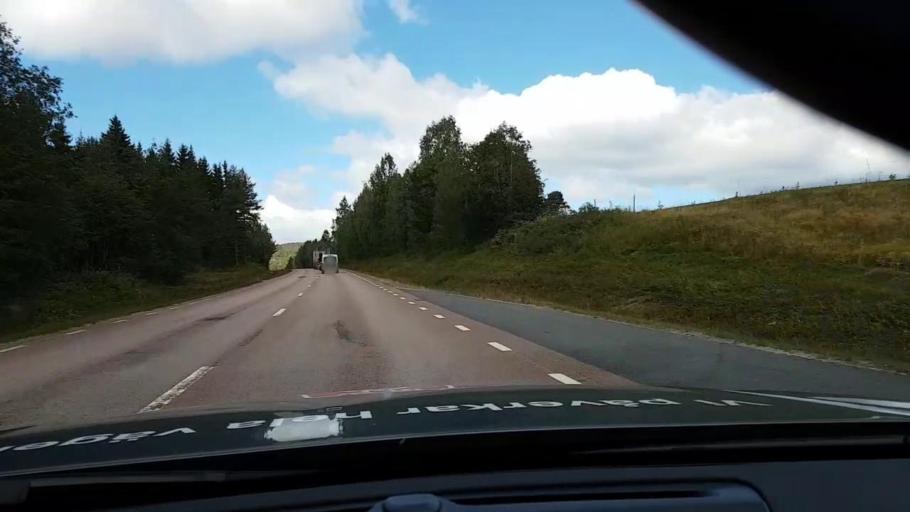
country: SE
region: Vaesternorrland
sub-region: OErnskoeldsviks Kommun
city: Bjasta
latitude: 63.3731
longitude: 18.4344
